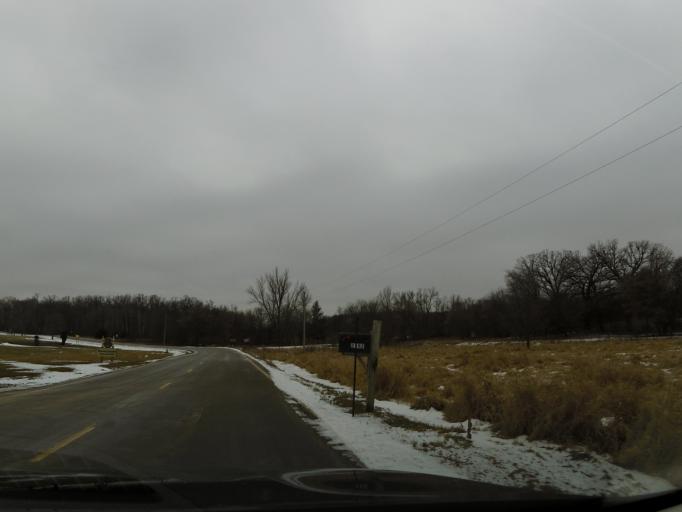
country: US
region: Minnesota
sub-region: Hennepin County
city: Medina
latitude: 45.0188
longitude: -93.6145
